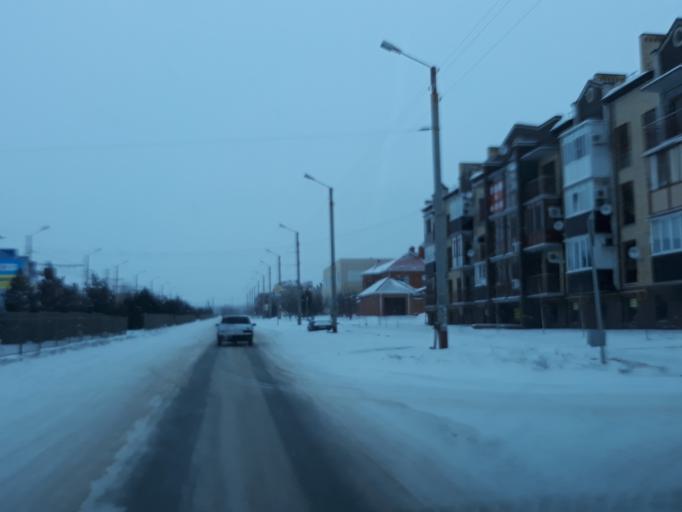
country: RU
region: Rostov
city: Taganrog
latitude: 47.2736
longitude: 38.9184
